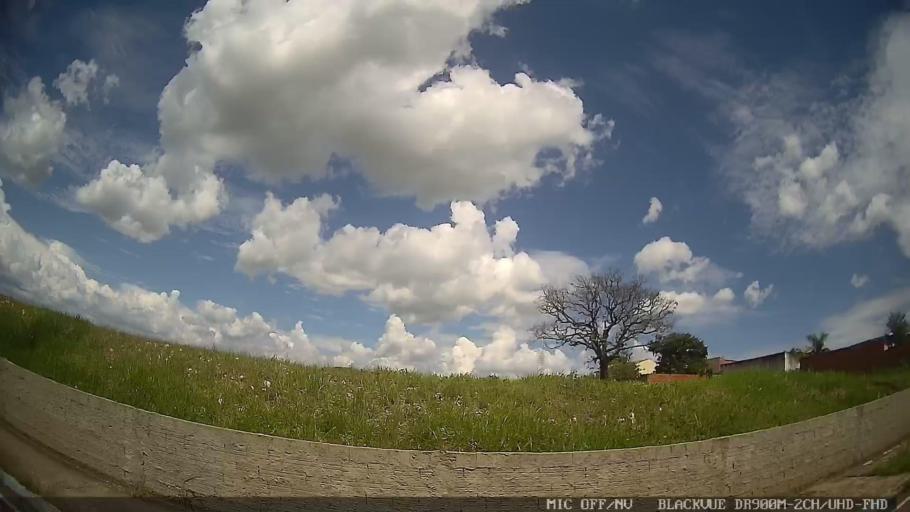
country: BR
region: Sao Paulo
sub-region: Conchas
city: Conchas
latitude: -23.0214
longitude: -48.0111
